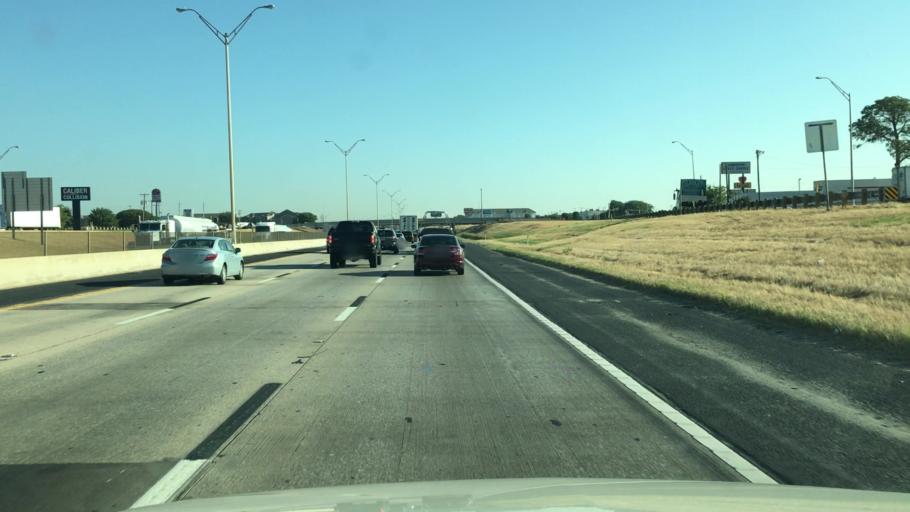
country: US
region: Texas
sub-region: Tarrant County
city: Crowley
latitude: 32.5954
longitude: -97.3193
